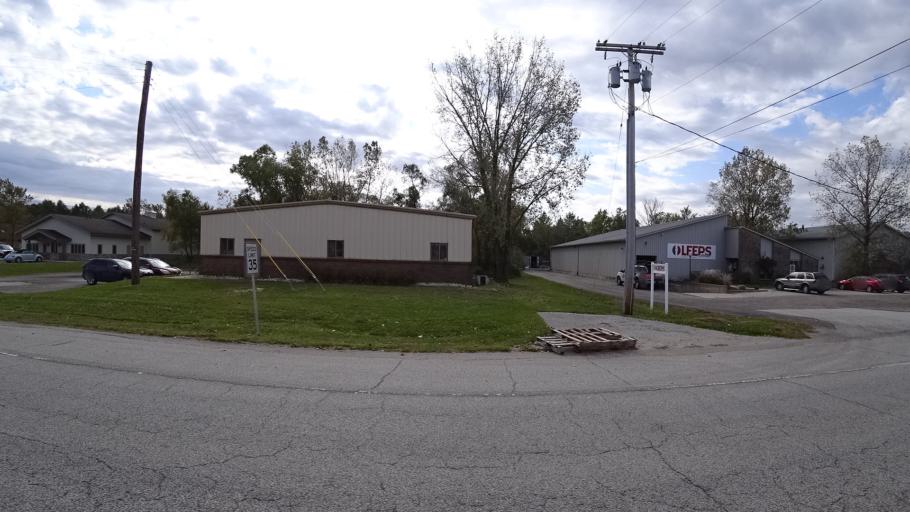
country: US
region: Indiana
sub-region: LaPorte County
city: Michigan City
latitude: 41.6659
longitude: -86.9025
